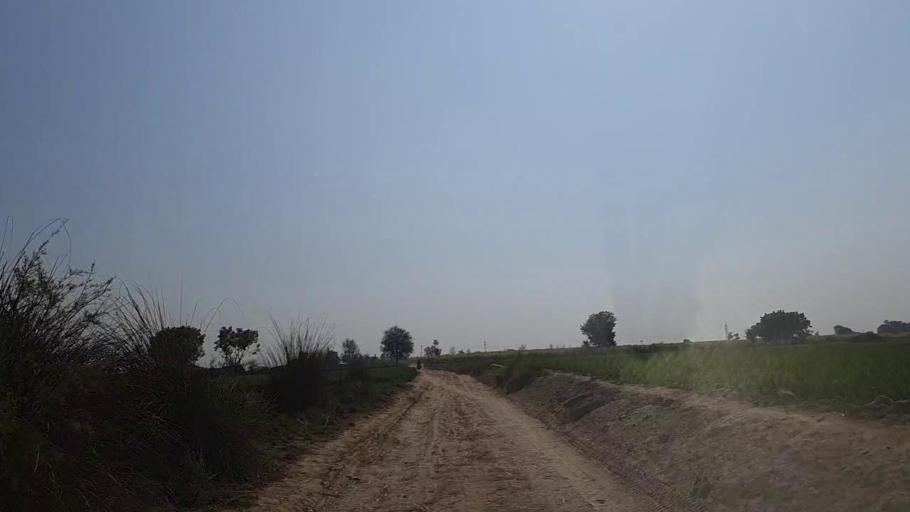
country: PK
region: Sindh
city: Moro
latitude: 26.6976
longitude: 67.9276
